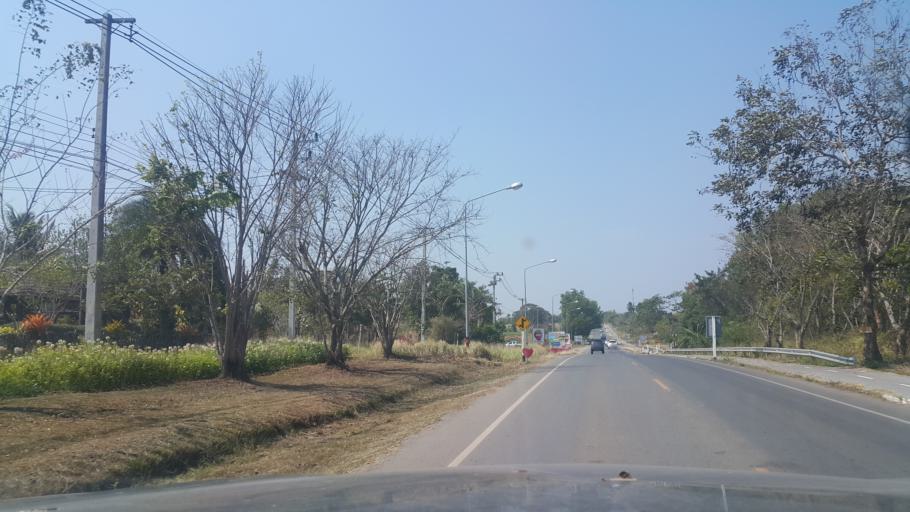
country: TH
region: Nakhon Ratchasima
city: Wang Nam Khiao
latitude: 14.3631
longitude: 101.9131
